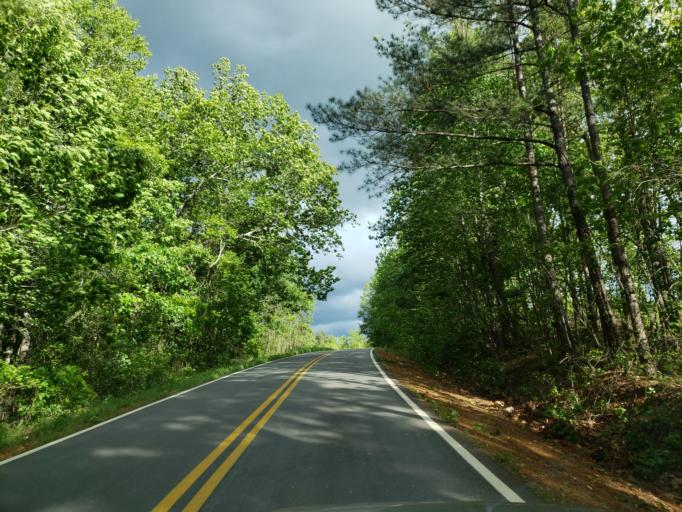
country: US
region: Georgia
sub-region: Haralson County
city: Tallapoosa
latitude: 33.8635
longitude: -85.3468
